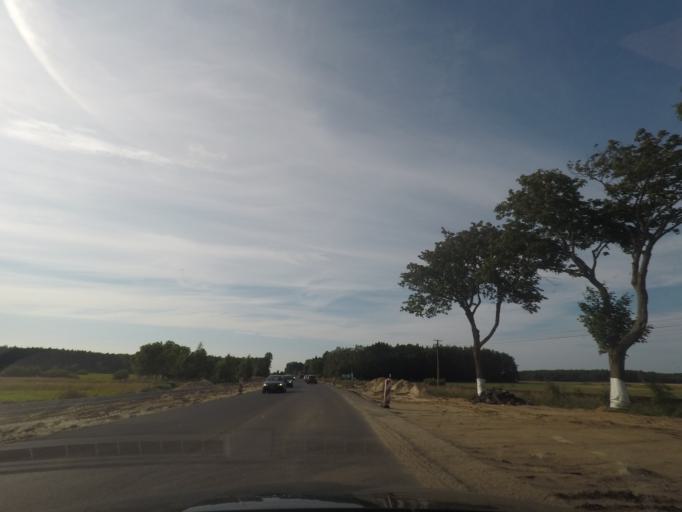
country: PL
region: Pomeranian Voivodeship
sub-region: Powiat leborski
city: Leba
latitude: 54.7290
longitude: 17.5675
